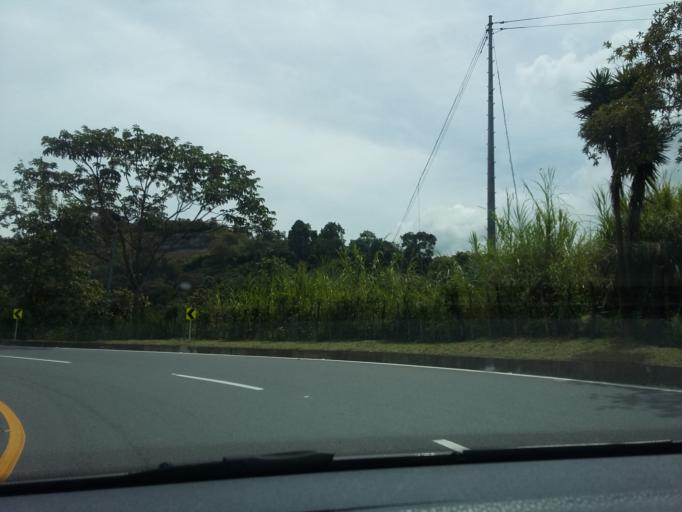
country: CO
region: Santander
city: Bucaramanga
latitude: 7.1135
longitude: -73.0786
